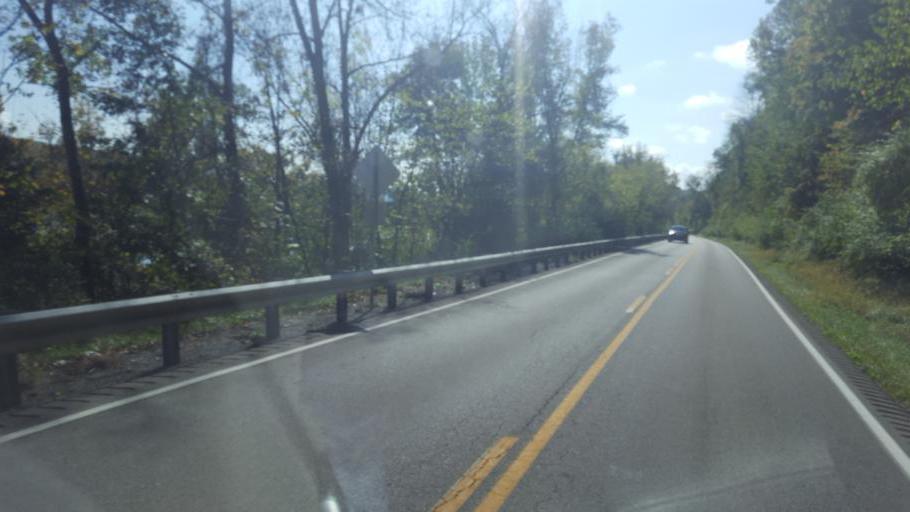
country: US
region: Ohio
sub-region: Brown County
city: Aberdeen
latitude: 38.6703
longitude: -83.7820
